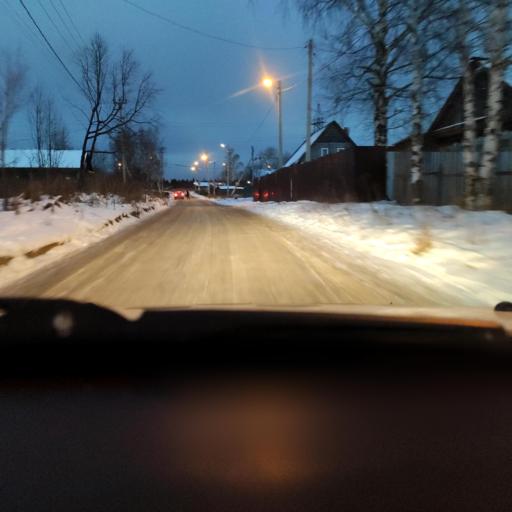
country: RU
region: Perm
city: Perm
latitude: 58.0391
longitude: 56.4001
